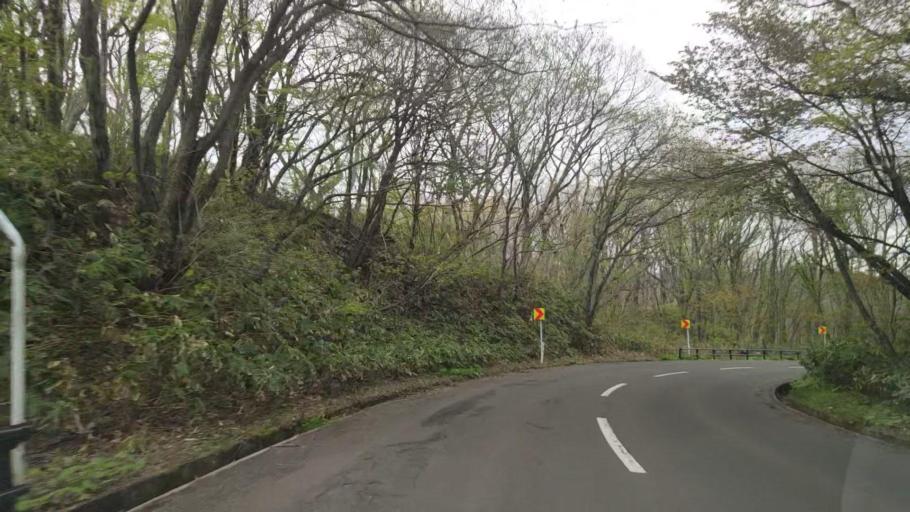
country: JP
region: Akita
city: Hanawa
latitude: 40.3736
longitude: 140.7904
